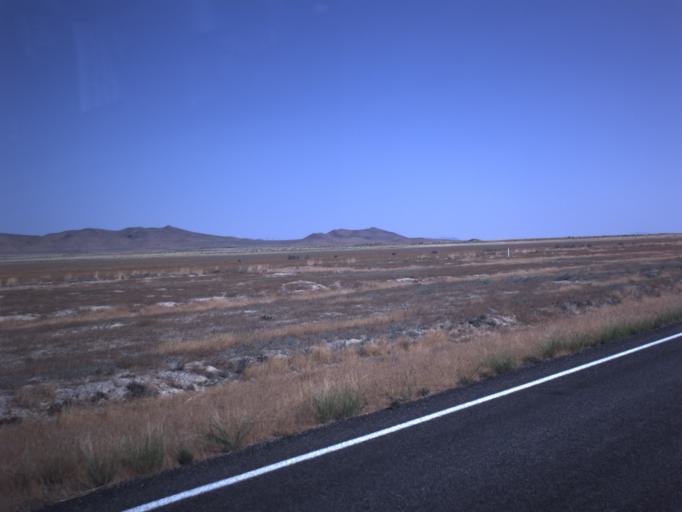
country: US
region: Utah
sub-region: Millard County
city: Delta
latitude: 38.9738
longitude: -112.7980
